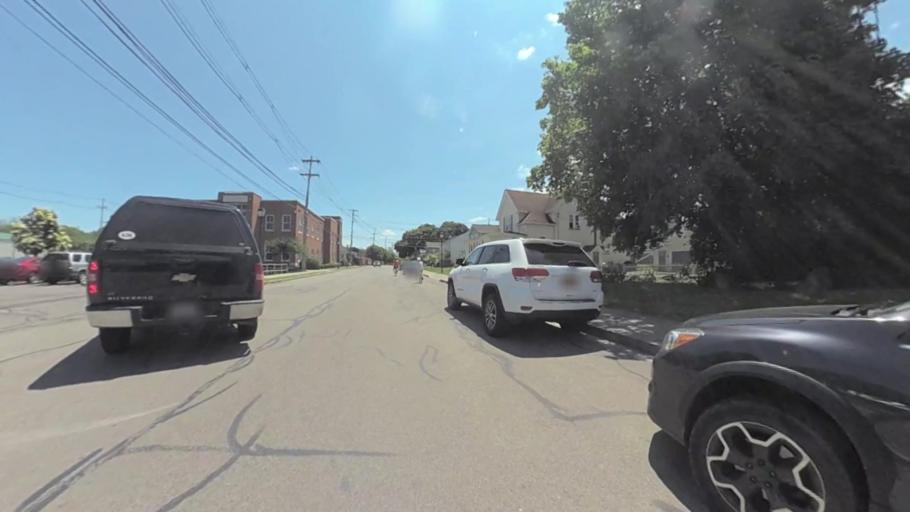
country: US
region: New York
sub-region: Monroe County
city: Fairport
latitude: 43.1014
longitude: -77.4395
